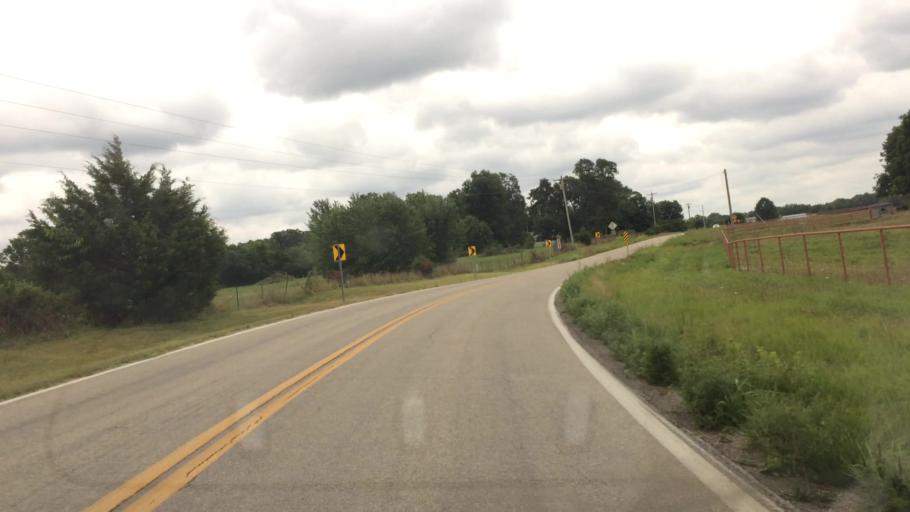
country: US
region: Missouri
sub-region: Greene County
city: Strafford
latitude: 37.2993
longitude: -93.1218
